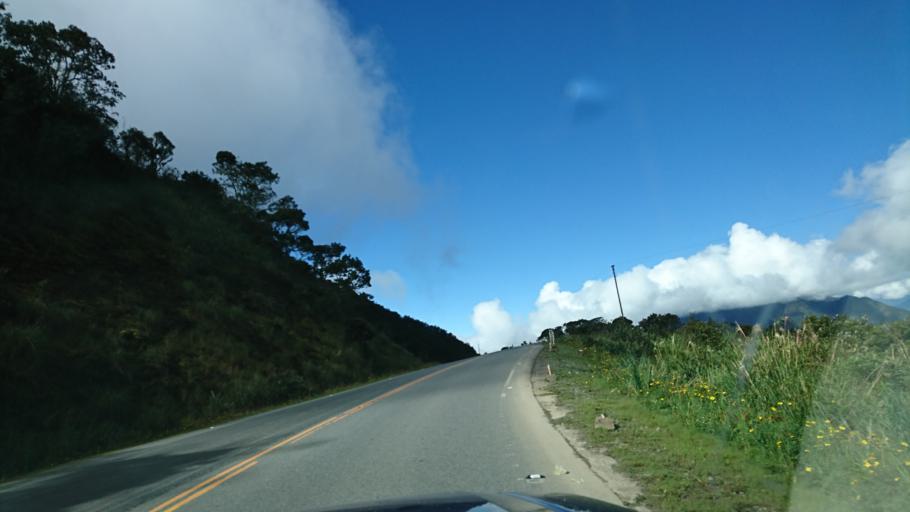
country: BO
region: La Paz
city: Coroico
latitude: -16.2916
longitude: -67.8625
